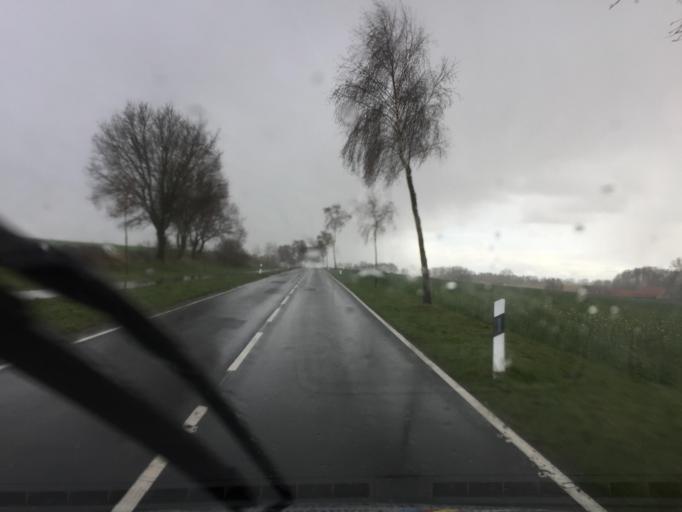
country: DE
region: Lower Saxony
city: Syke
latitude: 52.9289
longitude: 8.8830
